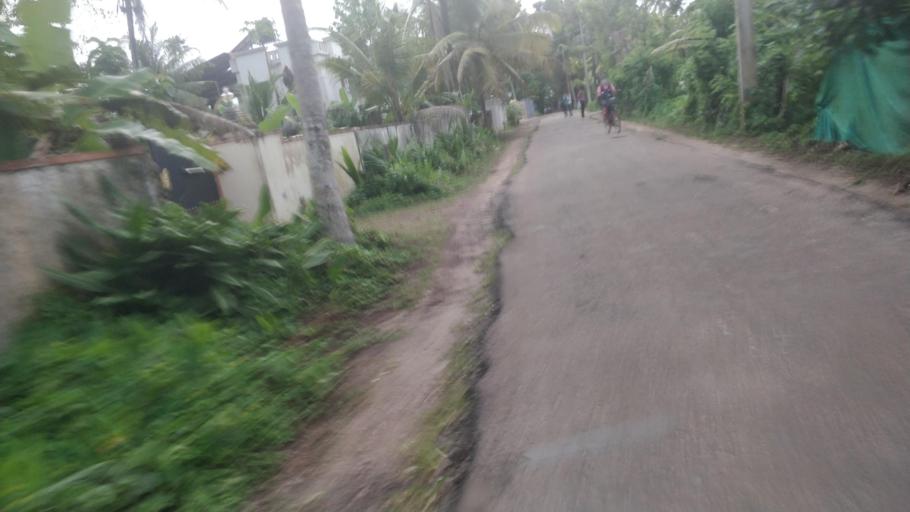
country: IN
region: Kerala
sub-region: Alappuzha
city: Shertallai
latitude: 9.6916
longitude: 76.3490
